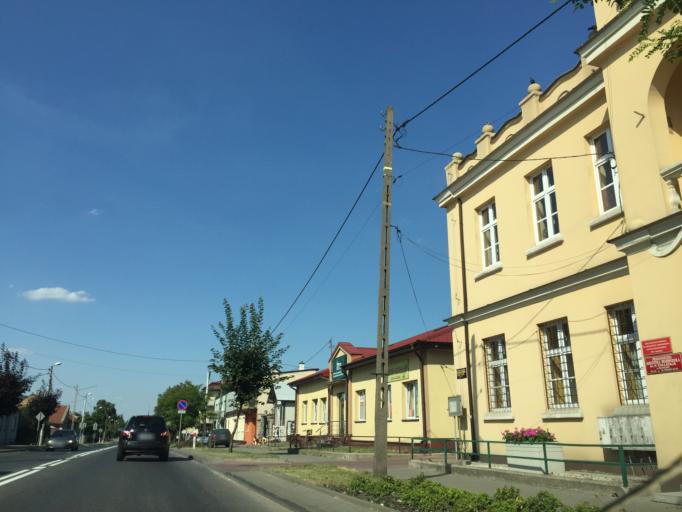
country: PL
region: Lesser Poland Voivodeship
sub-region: Powiat krakowski
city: Slomniki
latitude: 50.2424
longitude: 20.0826
